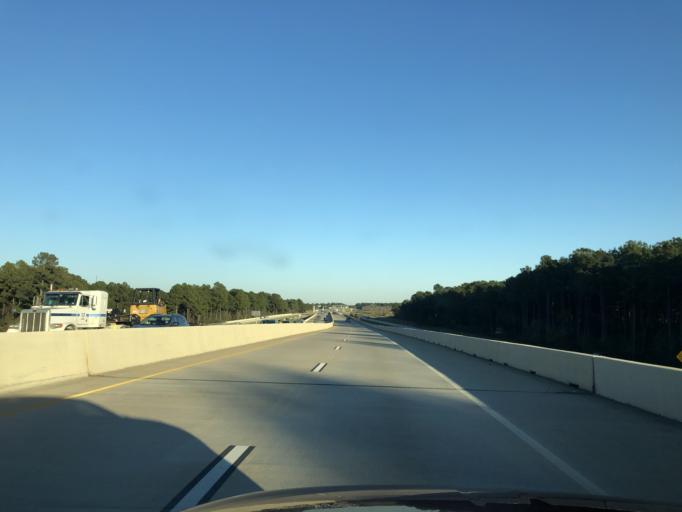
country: US
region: Texas
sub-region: Harris County
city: Tomball
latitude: 30.0506
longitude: -95.6587
